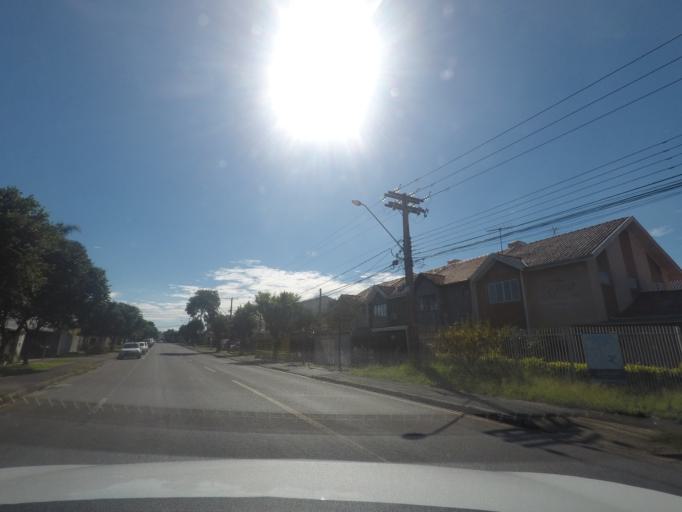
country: BR
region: Parana
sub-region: Sao Jose Dos Pinhais
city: Sao Jose dos Pinhais
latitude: -25.5051
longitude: -49.2736
